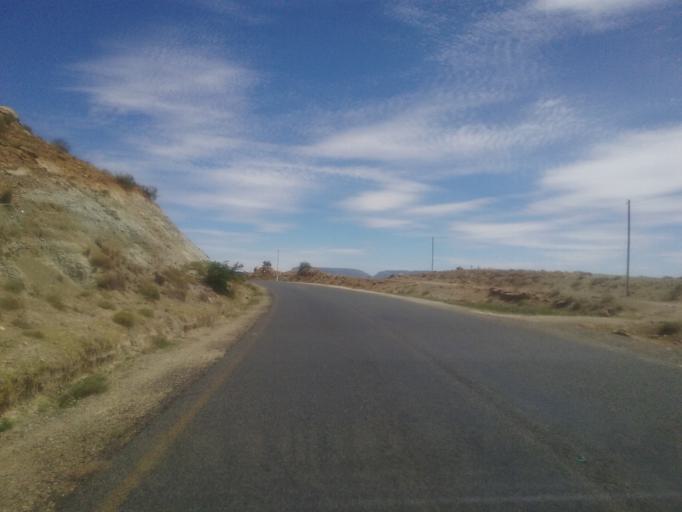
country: LS
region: Mohale's Hoek District
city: Mohale's Hoek
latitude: -30.0653
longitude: 27.4199
